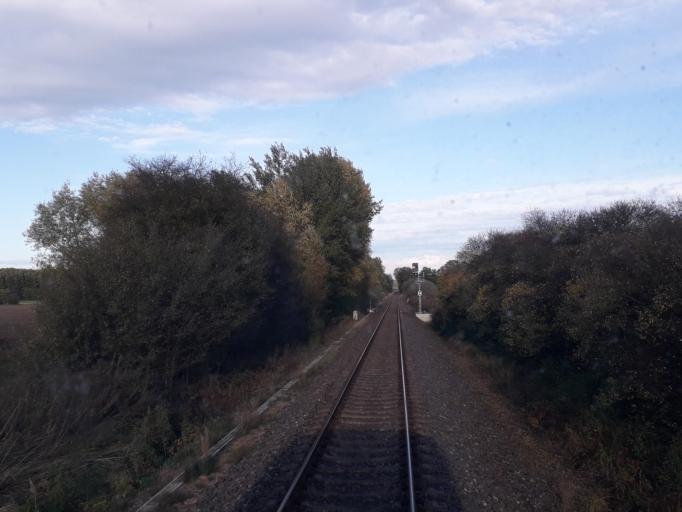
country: DE
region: Brandenburg
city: Perleberg
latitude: 53.0729
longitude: 11.8943
